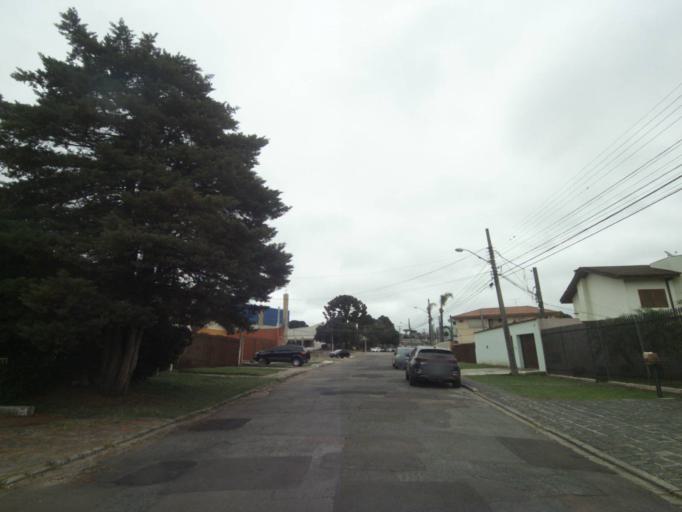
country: BR
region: Parana
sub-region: Curitiba
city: Curitiba
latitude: -25.4705
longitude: -49.2780
